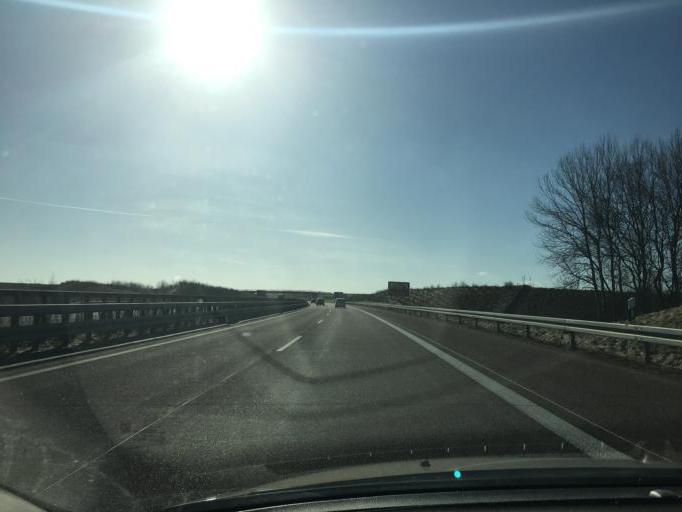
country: DE
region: Saxony
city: Niederfrohna
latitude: 50.9119
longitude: 12.7038
